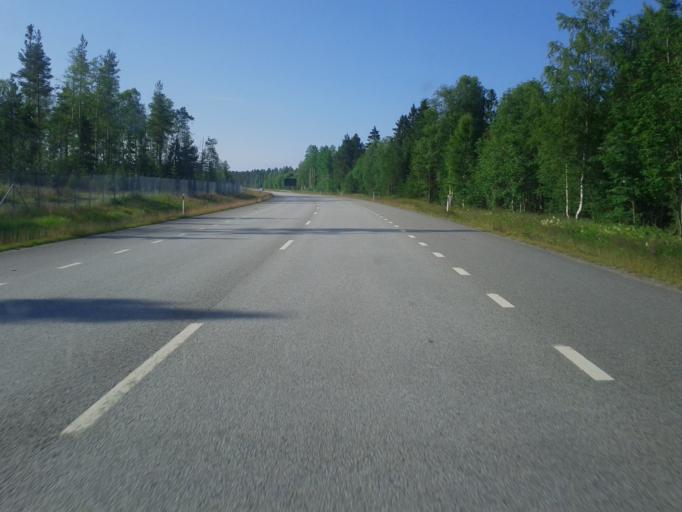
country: SE
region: Vaesterbotten
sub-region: Umea Kommun
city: Umea
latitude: 63.7856
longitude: 20.3034
